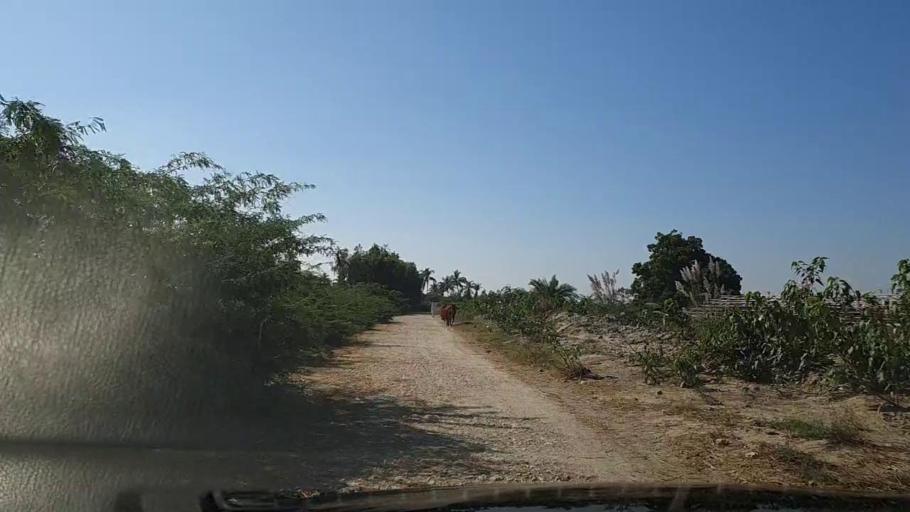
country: PK
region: Sindh
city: Thatta
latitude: 24.7131
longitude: 67.9192
